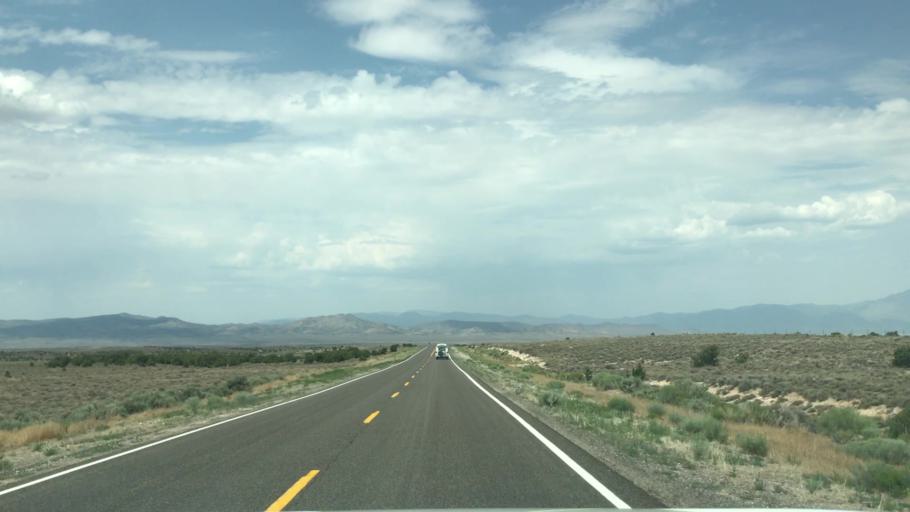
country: US
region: Nevada
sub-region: Eureka County
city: Eureka
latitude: 39.3927
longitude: -115.5141
